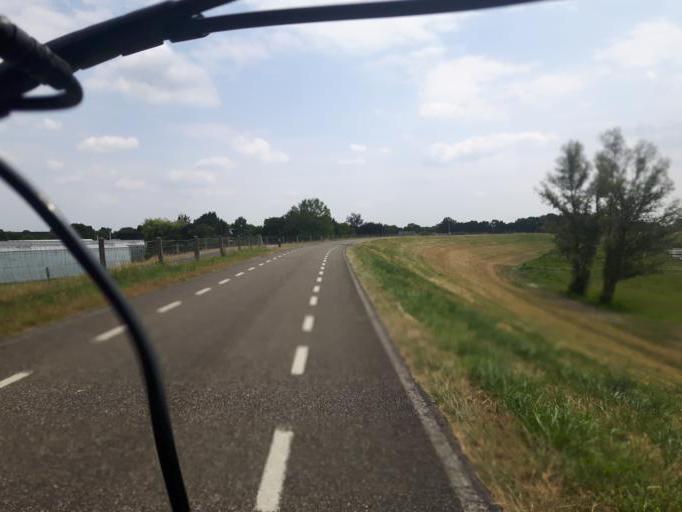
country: NL
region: Gelderland
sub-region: Gemeente Zaltbommel
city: Zaltbommel
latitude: 51.8225
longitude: 5.2033
